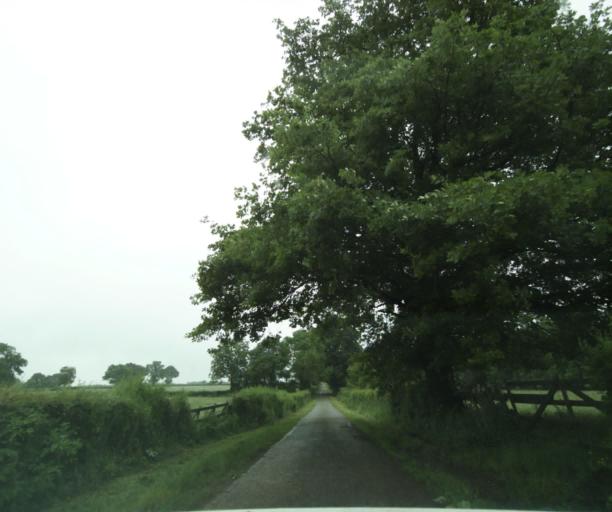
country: FR
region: Bourgogne
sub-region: Departement de Saone-et-Loire
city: Charolles
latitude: 46.4306
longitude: 4.3641
